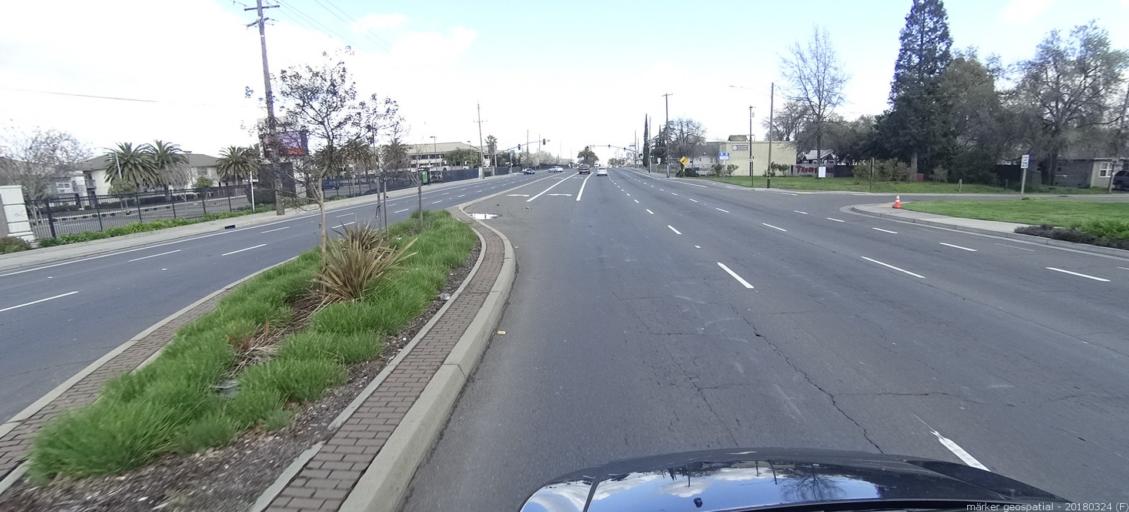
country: US
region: California
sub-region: Sacramento County
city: North Highlands
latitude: 38.6642
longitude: -121.3828
